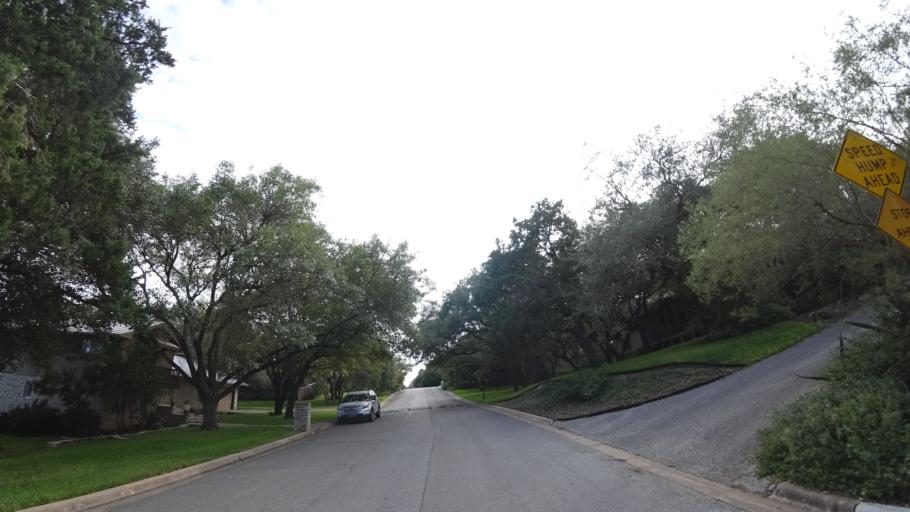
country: US
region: Texas
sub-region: Travis County
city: West Lake Hills
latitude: 30.2872
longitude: -97.7975
